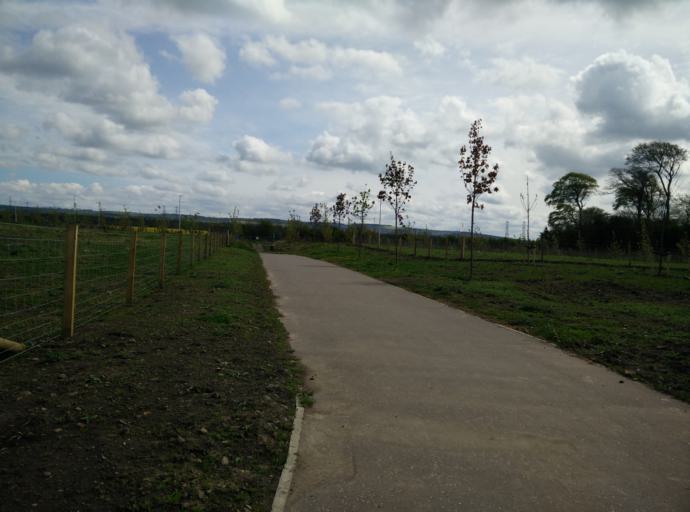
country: GB
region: Scotland
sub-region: Midlothian
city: Dalkeith
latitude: 55.9116
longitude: -3.0960
